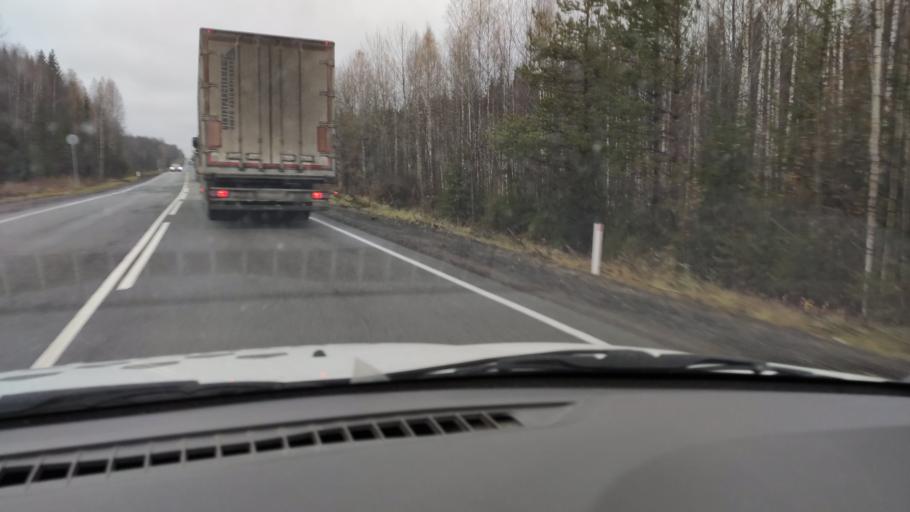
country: RU
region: Kirov
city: Omutninsk
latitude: 58.7542
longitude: 52.0451
